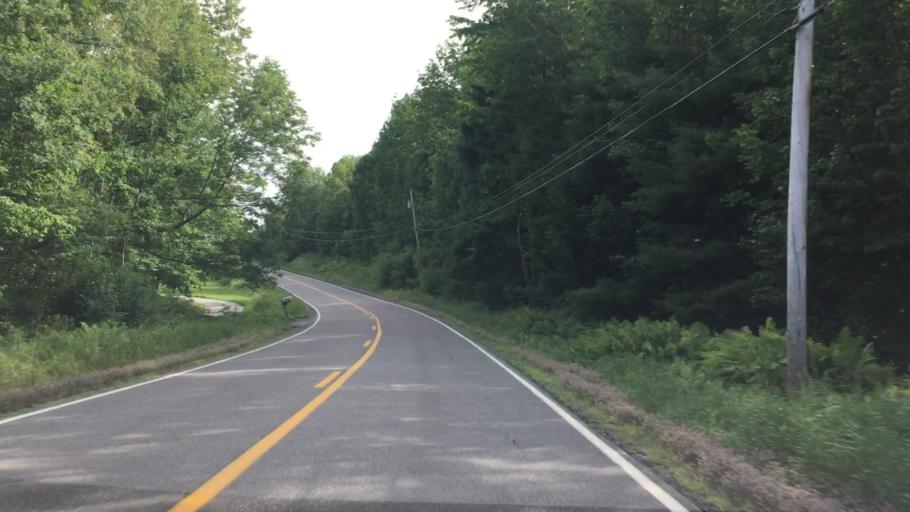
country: US
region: Maine
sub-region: Waldo County
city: Belfast
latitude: 44.3825
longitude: -69.0349
